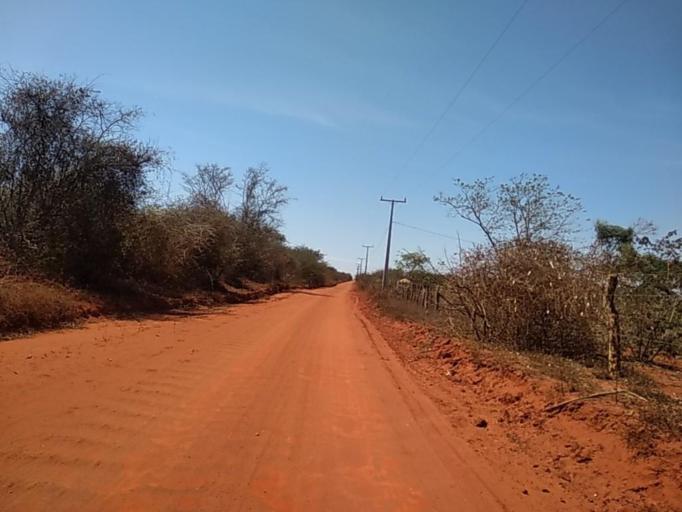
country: BR
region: Bahia
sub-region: Caetite
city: Caetite
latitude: -13.9833
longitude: -42.5106
